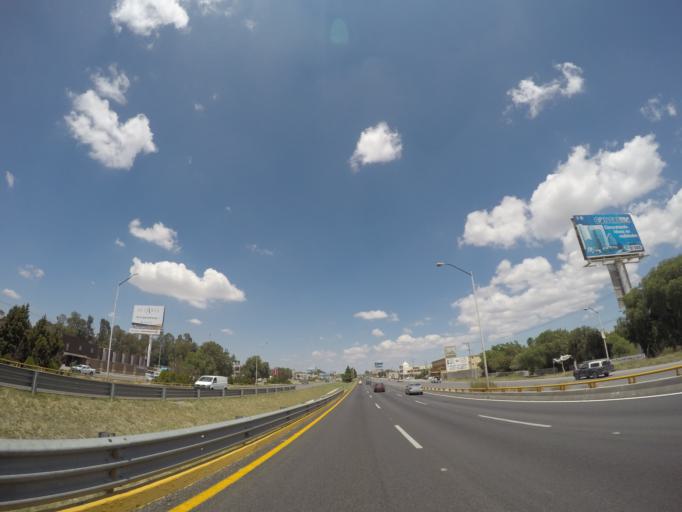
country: MX
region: San Luis Potosi
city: La Pila
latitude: 22.0850
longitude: -100.8789
